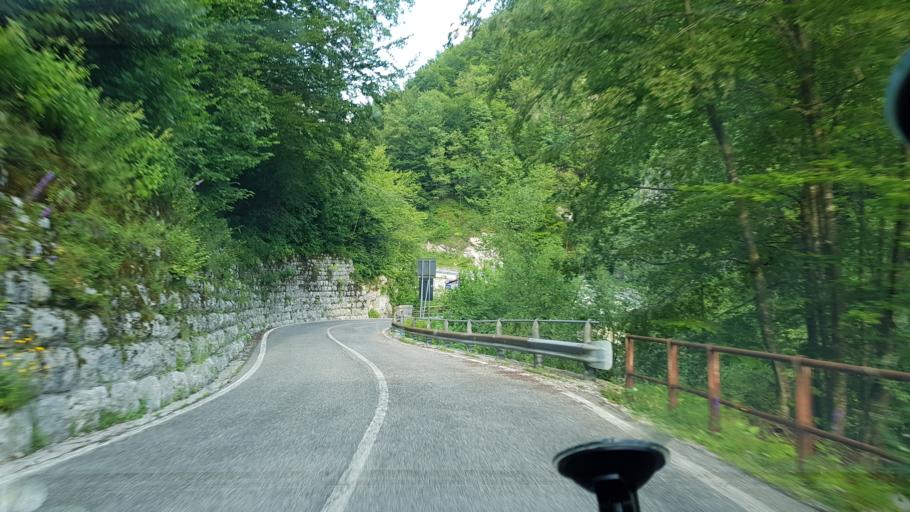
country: IT
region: Friuli Venezia Giulia
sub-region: Provincia di Udine
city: Taipana
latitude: 46.3058
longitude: 13.4164
